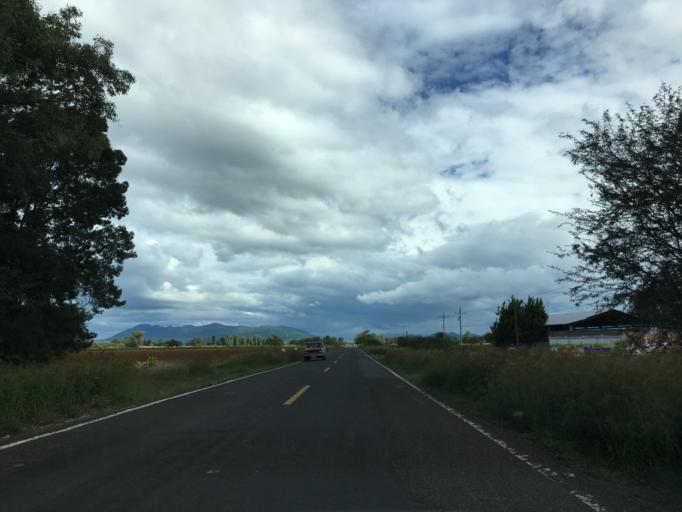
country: MX
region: Michoacan
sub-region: Cuitzeo
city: Cuamio
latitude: 20.0525
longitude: -101.0870
